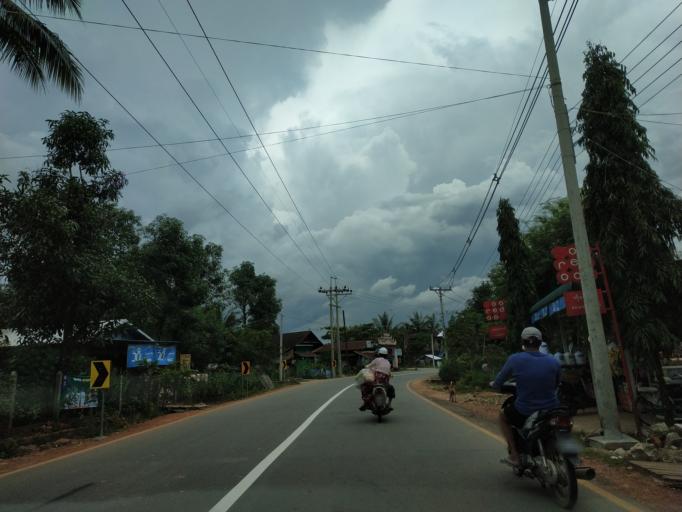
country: MM
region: Tanintharyi
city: Dawei
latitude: 14.0301
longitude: 98.2232
